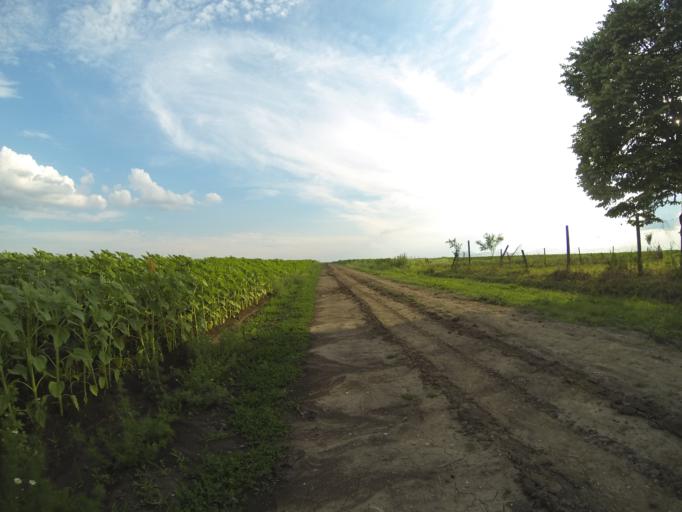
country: RO
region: Dolj
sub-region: Comuna Caloparu
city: Salcuta
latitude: 44.1428
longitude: 23.6942
